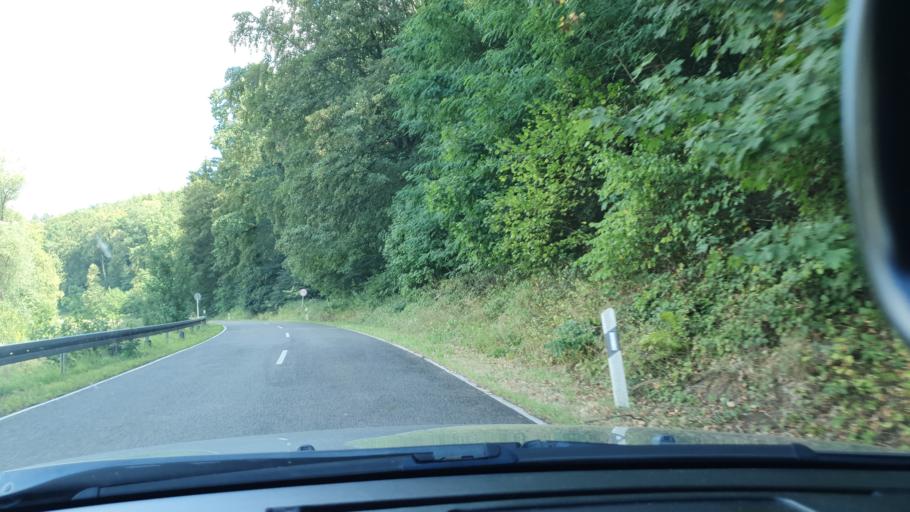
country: DE
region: Rheinland-Pfalz
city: Zweibrucken
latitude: 49.2514
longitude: 7.3892
